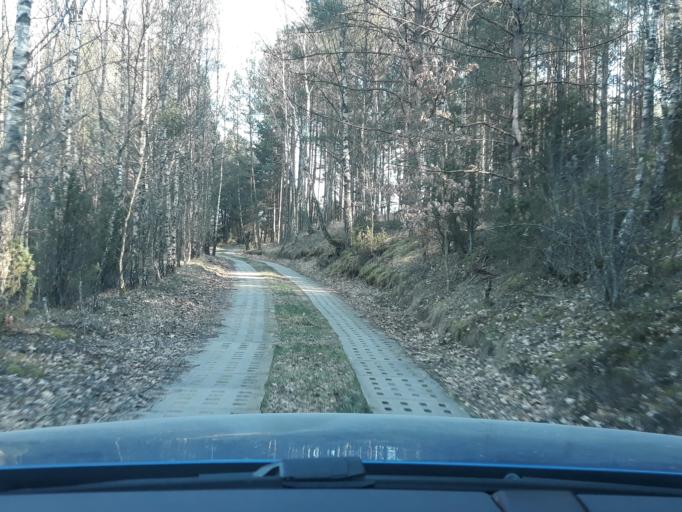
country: PL
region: Pomeranian Voivodeship
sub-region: Powiat bytowski
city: Lipnica
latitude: 53.9221
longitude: 17.4497
